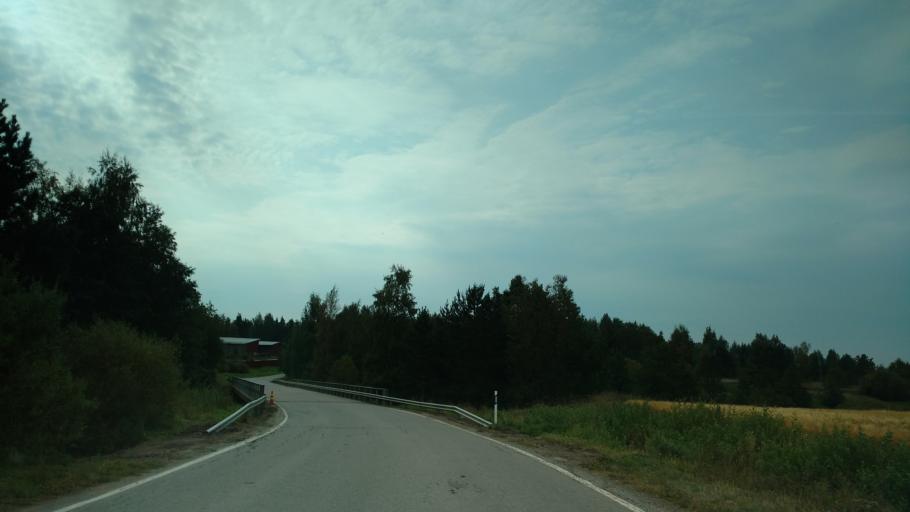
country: FI
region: Varsinais-Suomi
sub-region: Loimaa
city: Koski Tl
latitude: 60.6873
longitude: 23.1599
